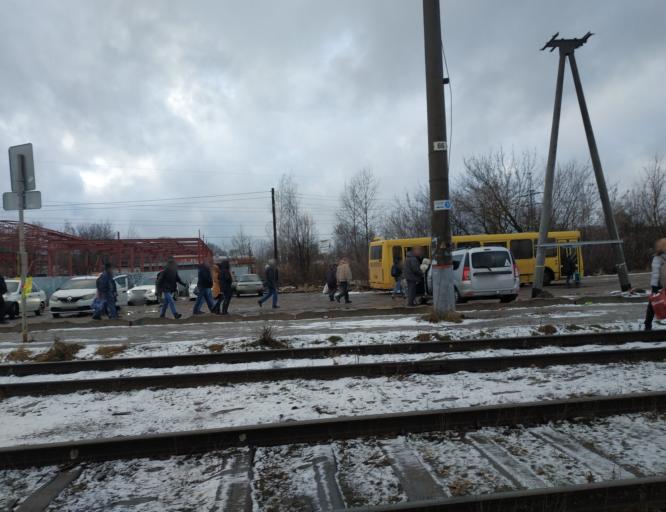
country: RU
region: Tverskaya
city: Kimry
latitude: 56.8545
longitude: 37.3766
